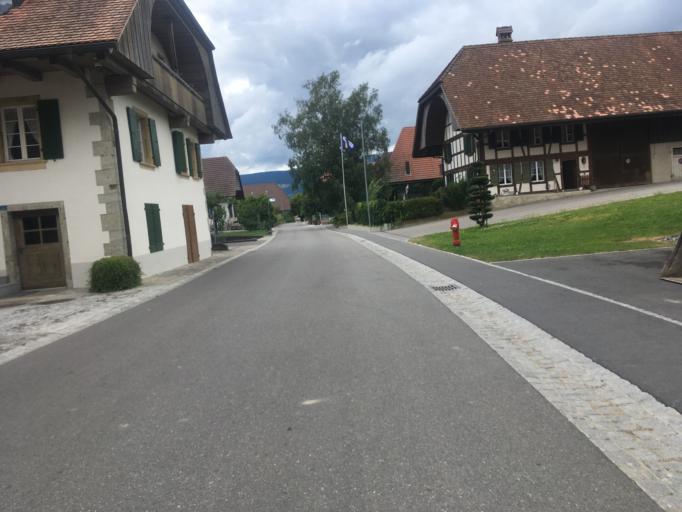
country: CH
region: Bern
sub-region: Seeland District
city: Erlach
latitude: 47.0320
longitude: 7.1121
